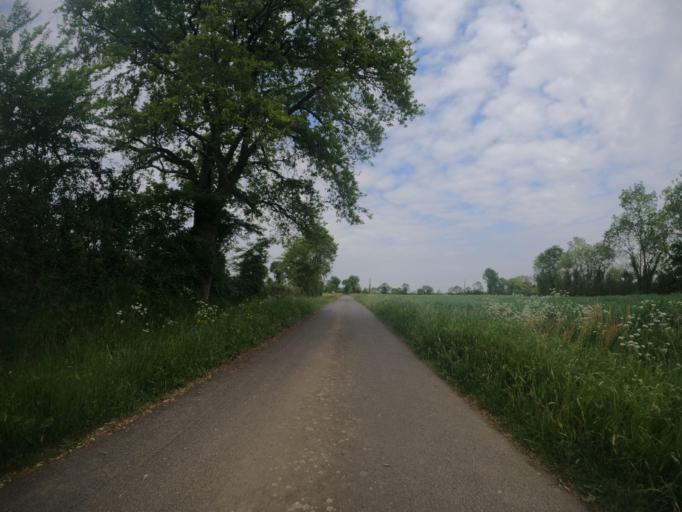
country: FR
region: Poitou-Charentes
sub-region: Departement des Deux-Sevres
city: Saint-Varent
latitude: 46.8758
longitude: -0.2831
